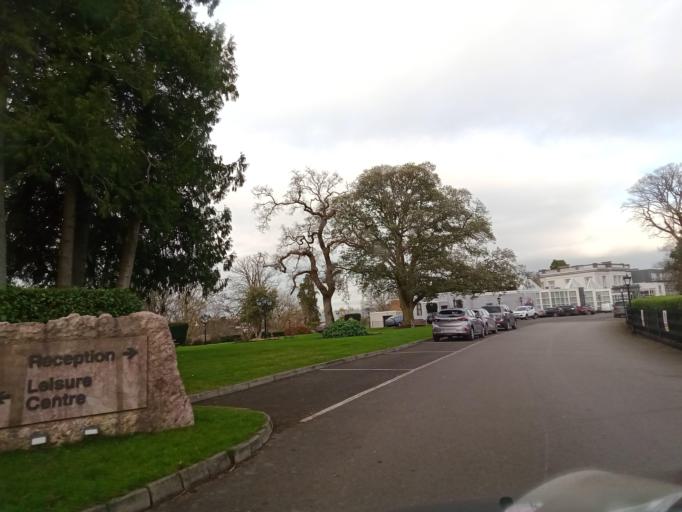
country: IE
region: Munster
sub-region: South Tipperary
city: Cluain Meala
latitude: 52.3523
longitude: -7.6862
